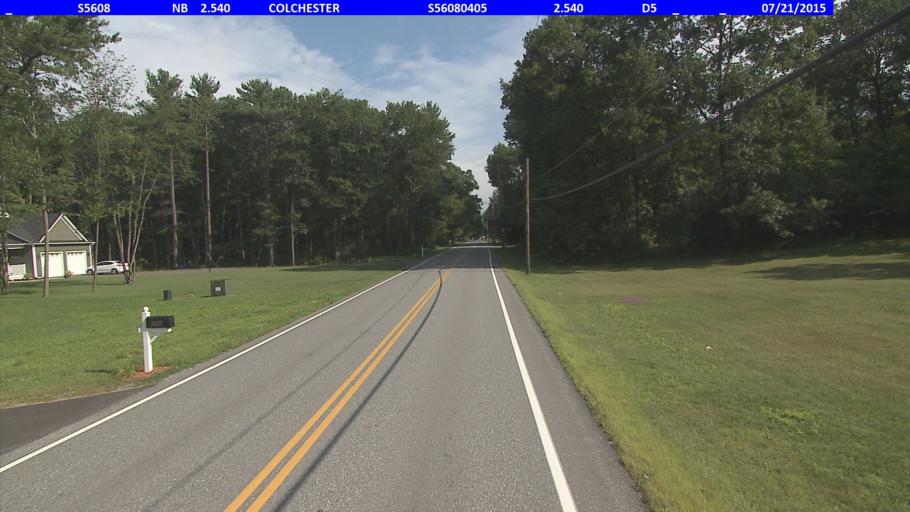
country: US
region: Vermont
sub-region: Chittenden County
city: Winooski
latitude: 44.5333
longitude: -73.2082
